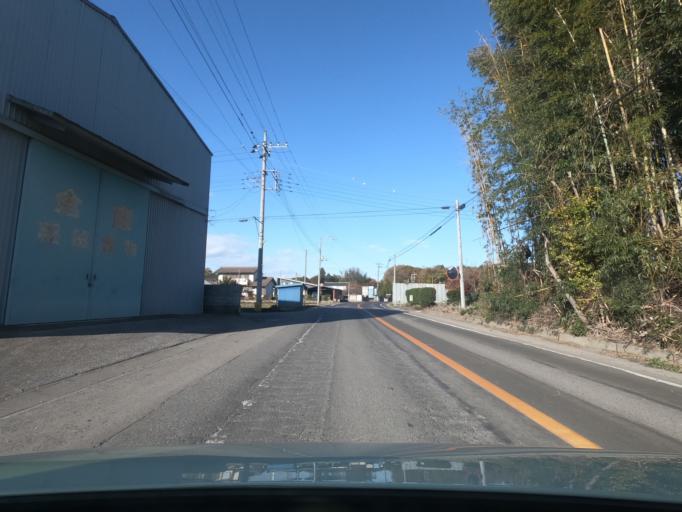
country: JP
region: Ibaraki
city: Koga
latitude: 36.2103
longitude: 139.7650
